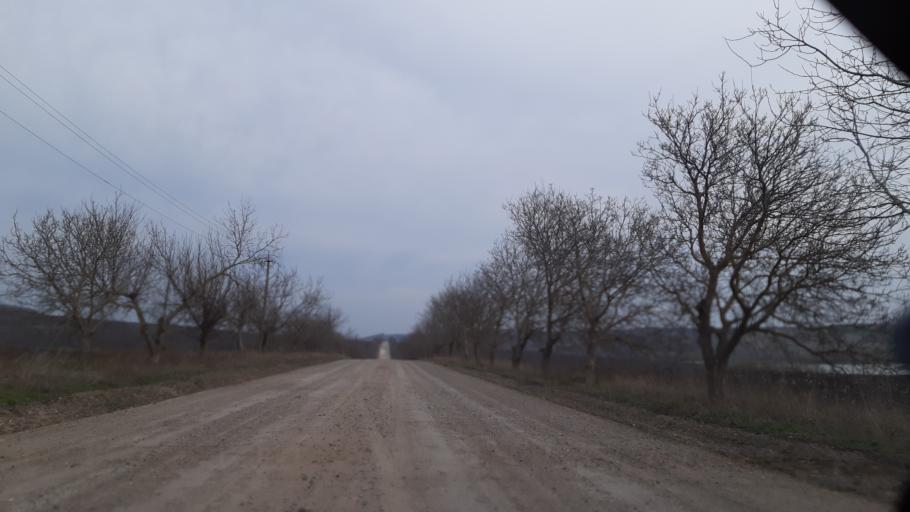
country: MD
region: Soldanesti
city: Soldanesti
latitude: 47.6998
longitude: 28.7243
